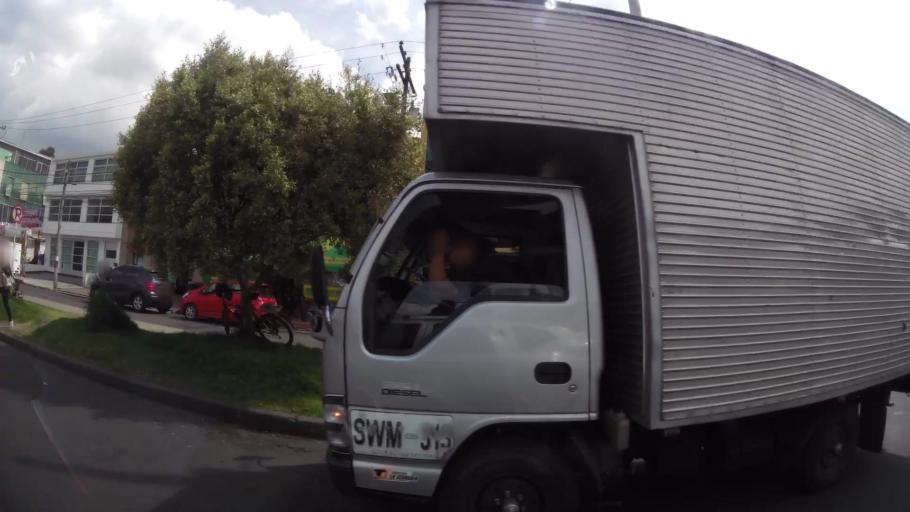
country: CO
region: Bogota D.C.
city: Bogota
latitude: 4.6014
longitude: -74.1103
